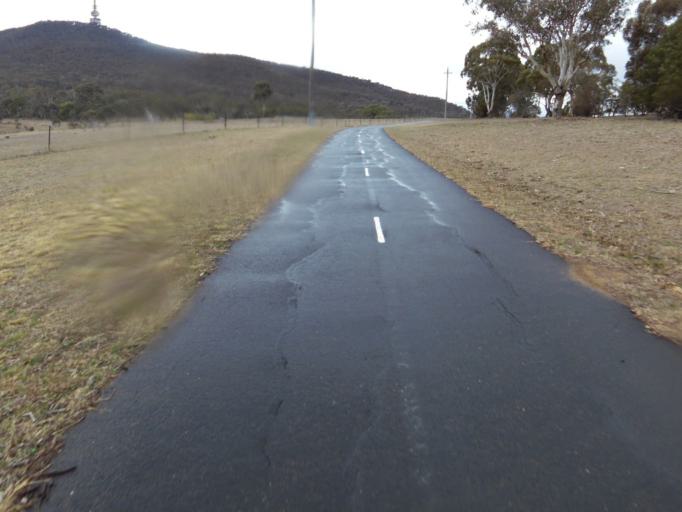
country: AU
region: Australian Capital Territory
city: Macquarie
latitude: -35.2772
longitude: 149.0794
